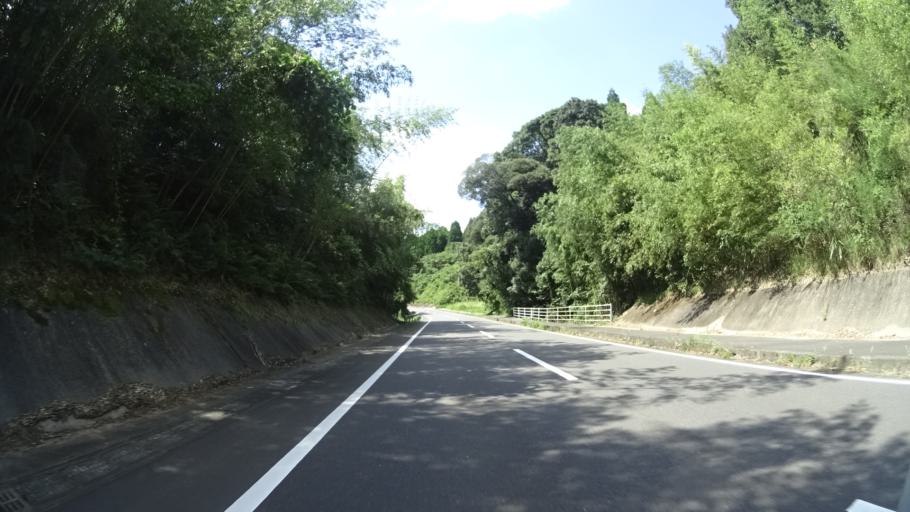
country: JP
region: Kagoshima
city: Kajiki
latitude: 31.8134
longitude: 130.6934
